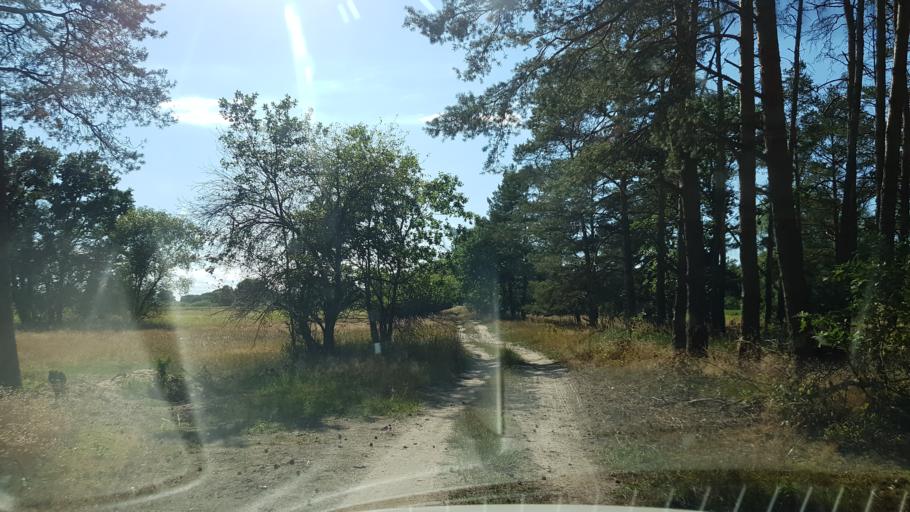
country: PL
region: West Pomeranian Voivodeship
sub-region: Powiat goleniowski
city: Goleniow
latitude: 53.5601
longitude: 14.7512
